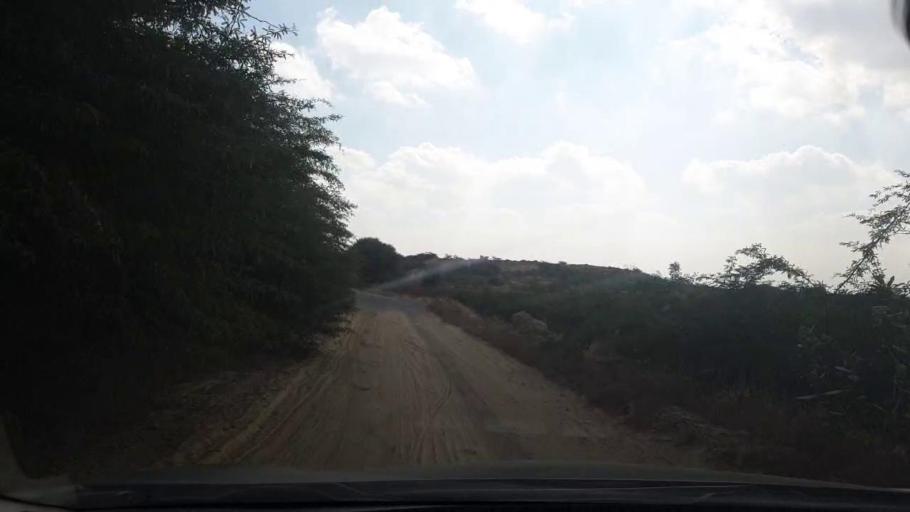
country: PK
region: Sindh
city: Malir Cantonment
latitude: 25.0257
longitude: 67.3495
